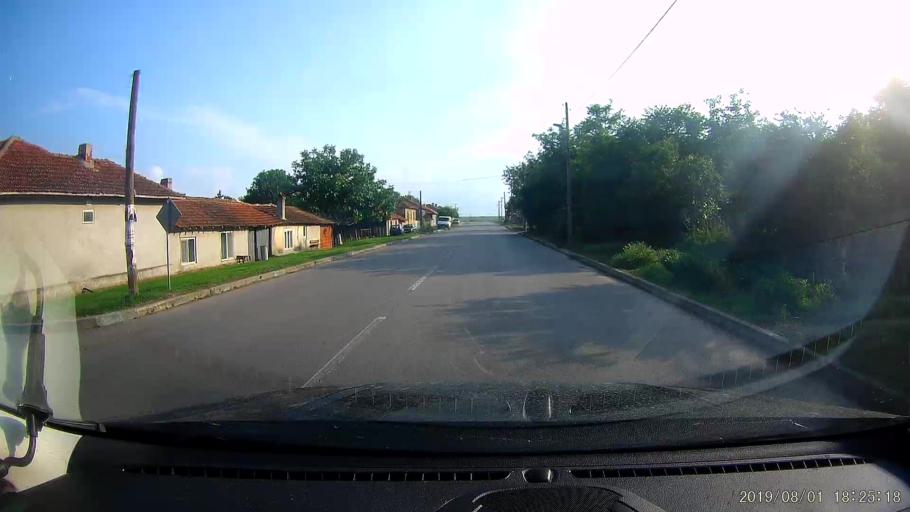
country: BG
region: Shumen
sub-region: Obshtina Venets
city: Venets
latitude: 43.6178
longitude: 26.9974
